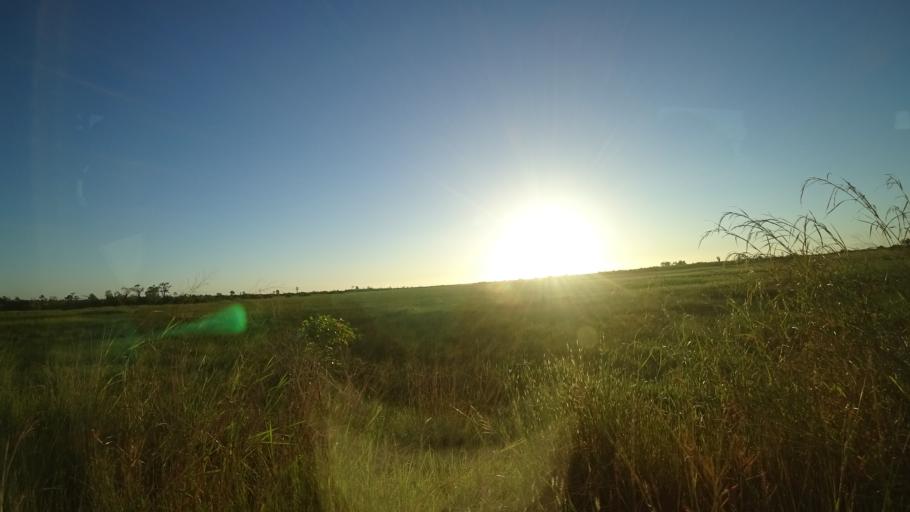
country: MZ
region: Sofala
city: Beira
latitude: -19.6281
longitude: 35.0602
